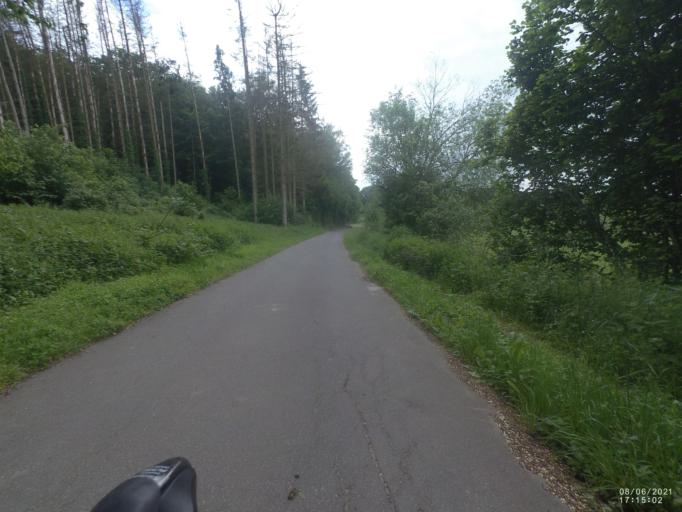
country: DE
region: Rheinland-Pfalz
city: Kalt
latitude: 50.2493
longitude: 7.3992
